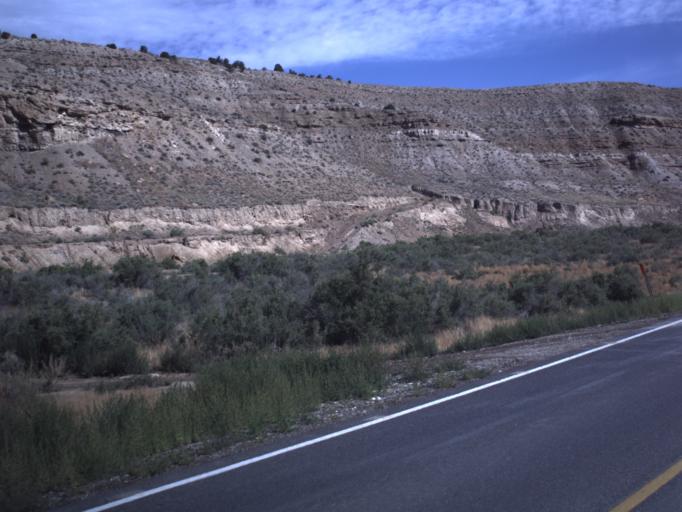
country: US
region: Utah
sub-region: Duchesne County
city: Duchesne
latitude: 40.1497
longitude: -110.4150
